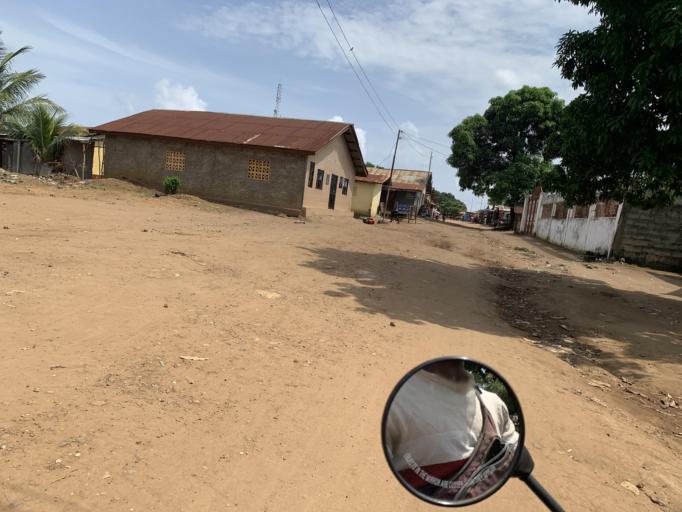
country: SL
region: Western Area
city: Hastings
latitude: 8.4087
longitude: -13.1343
